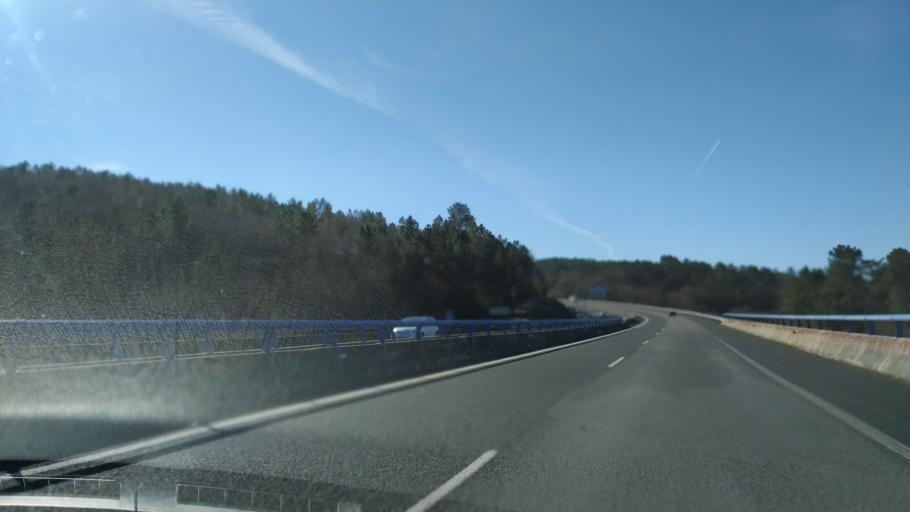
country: ES
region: Galicia
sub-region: Provincia de Pontevedra
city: Lalin
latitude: 42.6141
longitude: -8.0992
